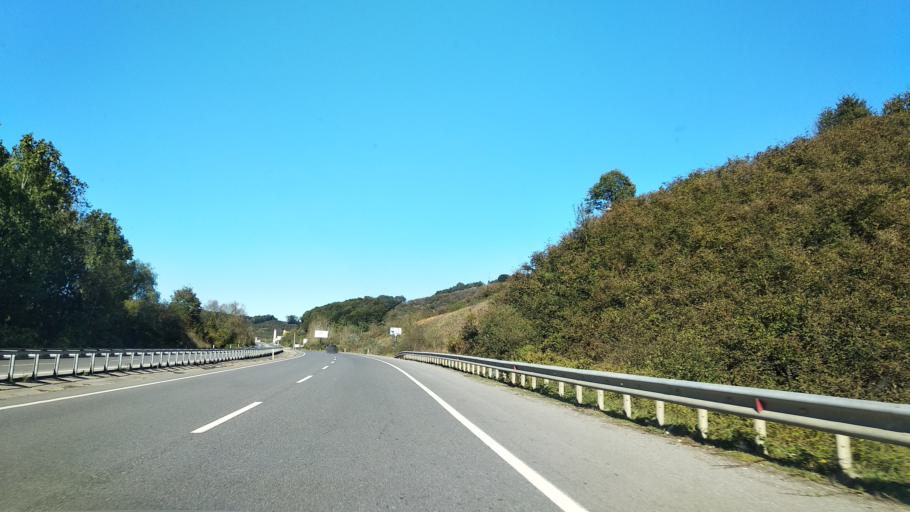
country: TR
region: Sakarya
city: Karasu
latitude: 41.0660
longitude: 30.6428
